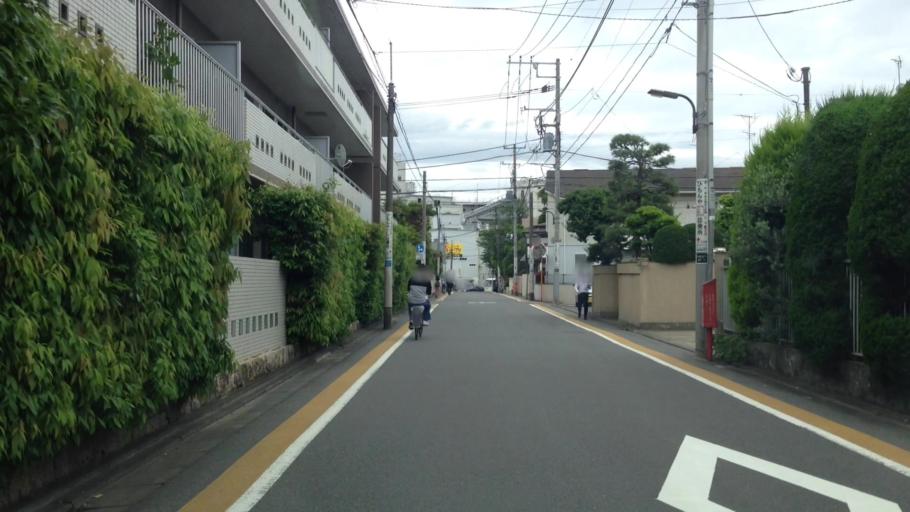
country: JP
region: Tokyo
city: Tokyo
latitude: 35.6257
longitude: 139.6865
